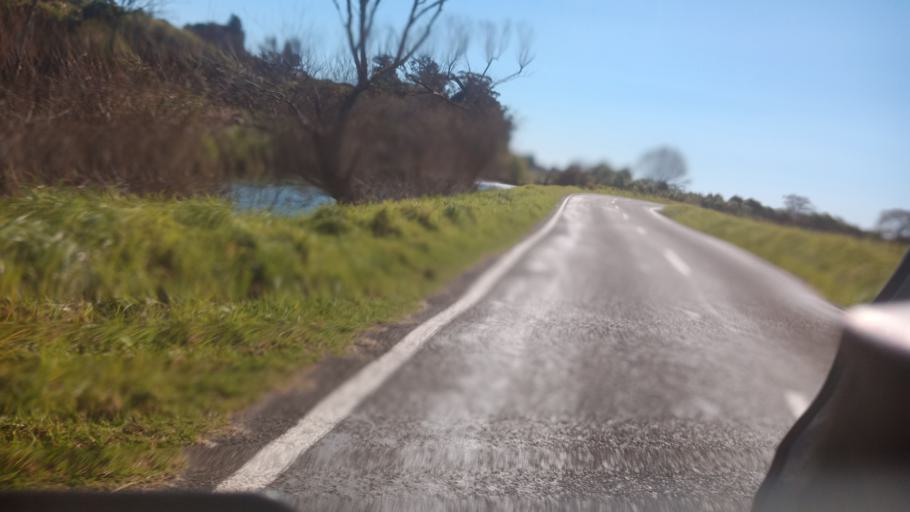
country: NZ
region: Bay of Plenty
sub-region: Opotiki District
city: Opotiki
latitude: -37.9923
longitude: 177.3889
